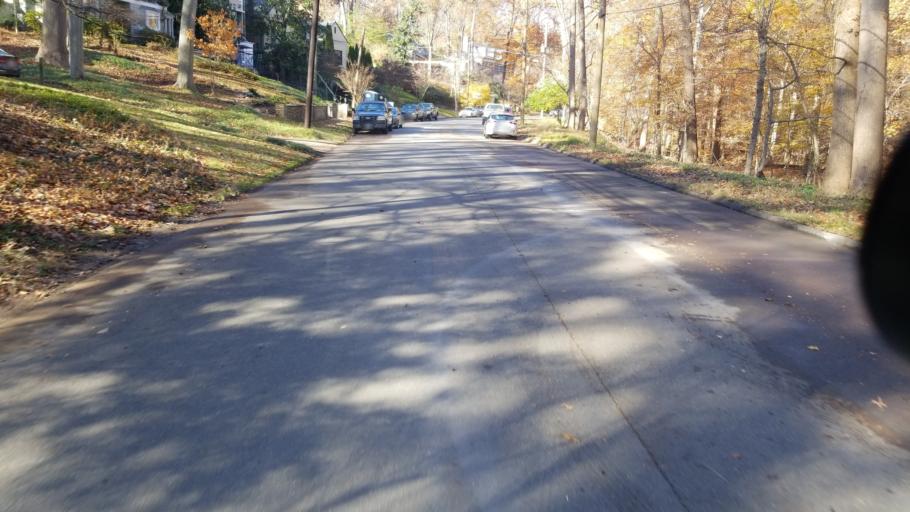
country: US
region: Maryland
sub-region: Montgomery County
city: Brookmont
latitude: 38.9214
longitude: -77.0864
